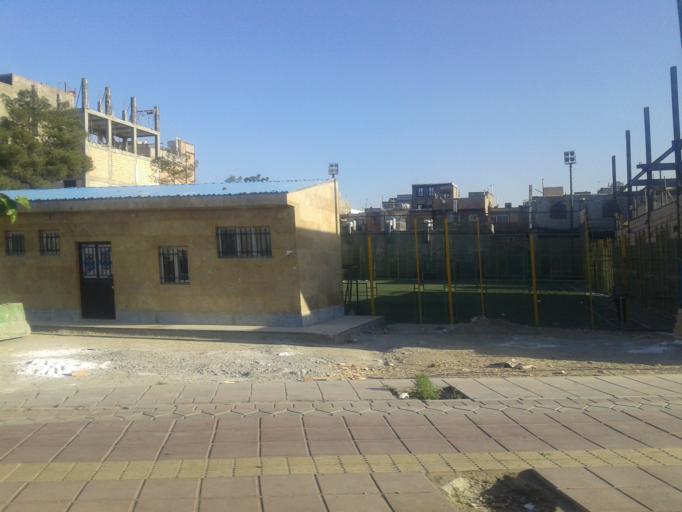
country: IR
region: Tehran
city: Rey
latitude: 35.6263
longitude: 51.3581
